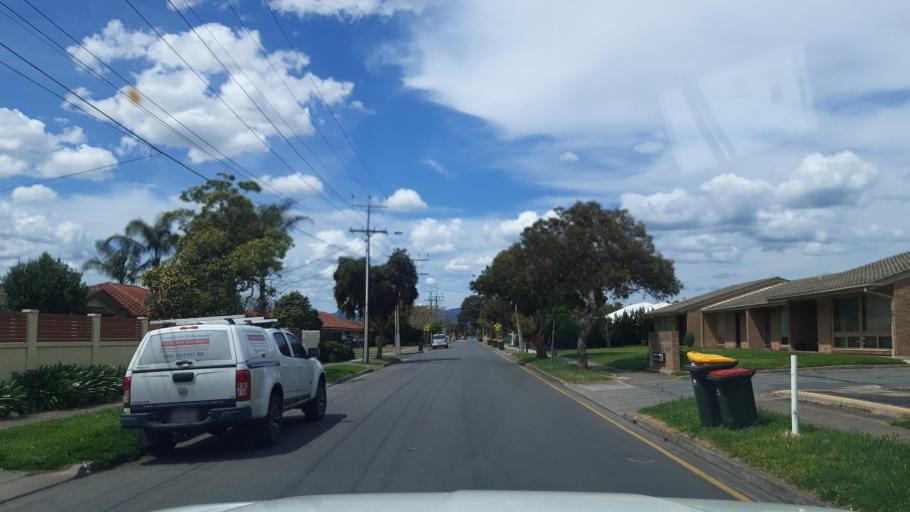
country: AU
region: South Australia
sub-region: Marion
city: Plympton Park
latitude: -34.9830
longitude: 138.5401
